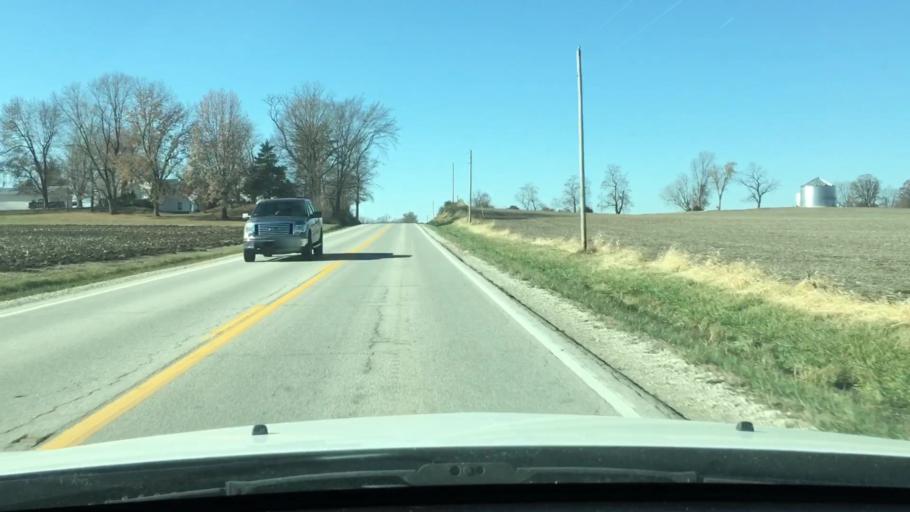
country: US
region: Illinois
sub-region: Pike County
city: Pittsfield
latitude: 39.6135
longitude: -90.7428
